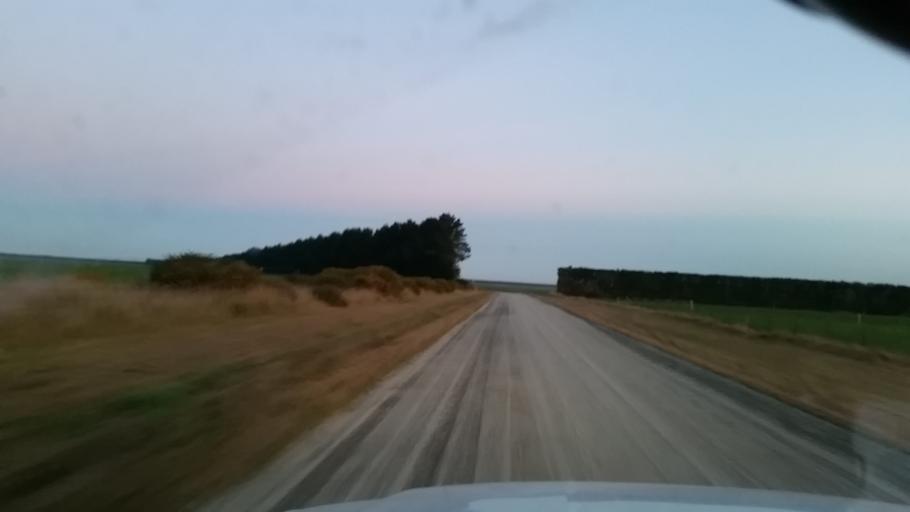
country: NZ
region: Canterbury
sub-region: Ashburton District
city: Tinwald
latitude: -43.9443
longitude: 171.6107
